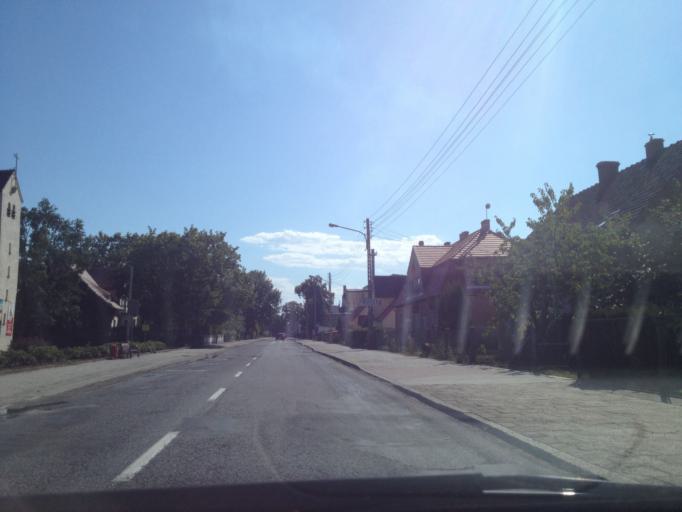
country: PL
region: Lubusz
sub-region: Powiat zaganski
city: Ilowa
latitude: 51.5062
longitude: 15.2026
